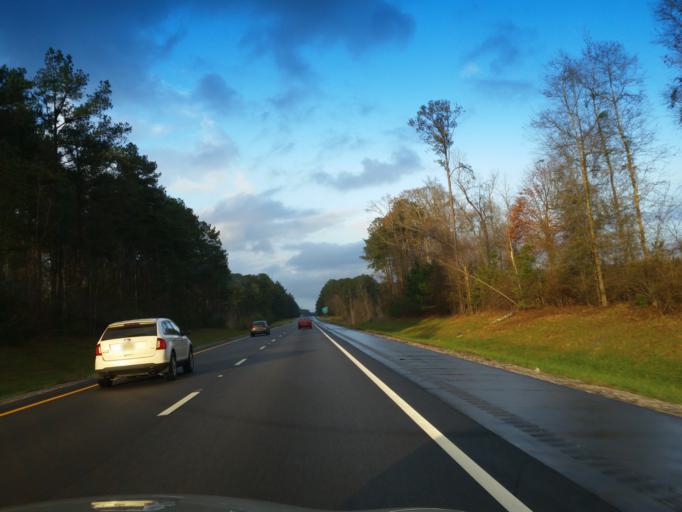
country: US
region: Mississippi
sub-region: Jones County
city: Sharon
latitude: 31.9473
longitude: -88.9833
